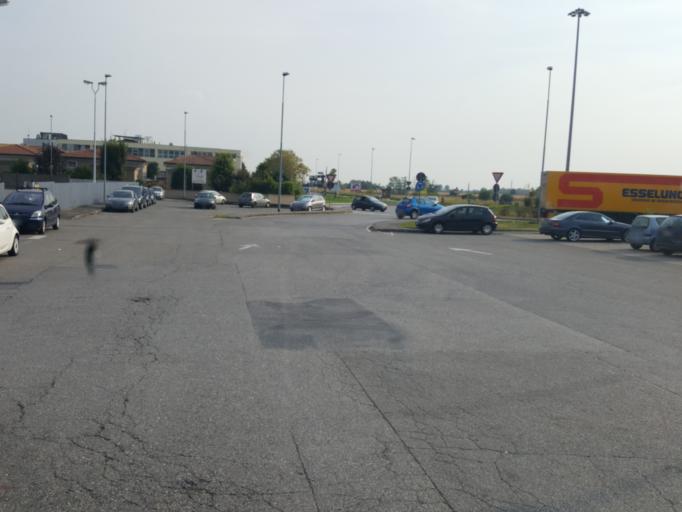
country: IT
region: Lombardy
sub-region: Provincia di Bergamo
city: Calcinate
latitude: 45.6176
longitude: 9.8078
